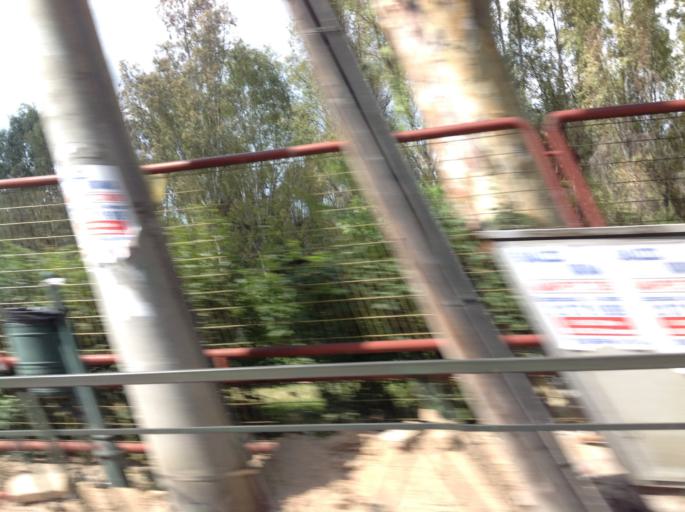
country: GR
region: Attica
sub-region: Nomarchia Athinas
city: Kaisariani
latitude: 37.9660
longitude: 23.7724
